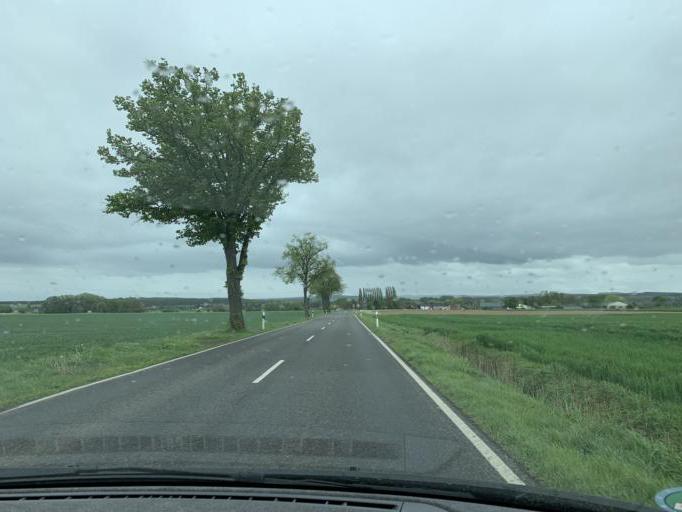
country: DE
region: North Rhine-Westphalia
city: Zulpich
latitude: 50.6763
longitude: 6.6442
